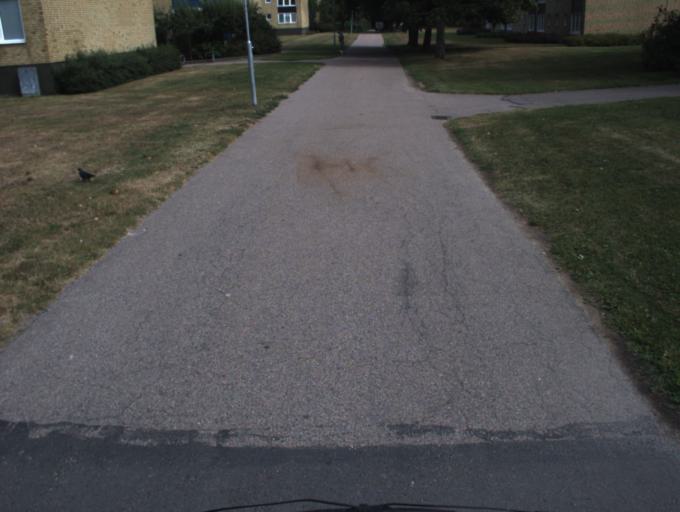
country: SE
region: Skane
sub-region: Helsingborg
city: Helsingborg
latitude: 56.0487
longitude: 12.7310
